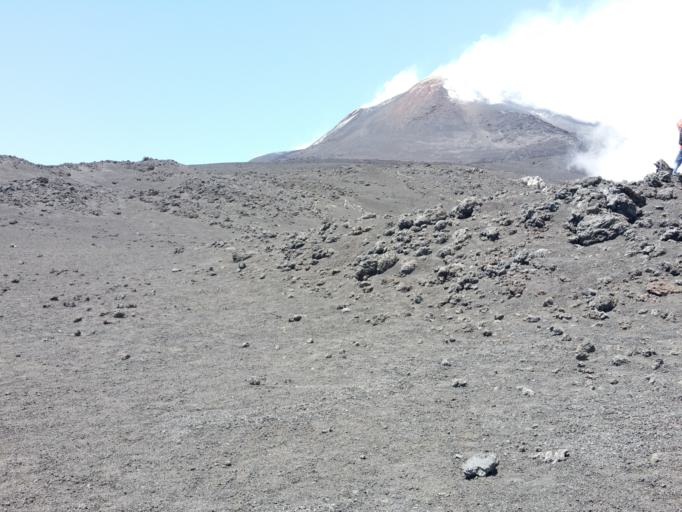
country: IT
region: Sicily
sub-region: Catania
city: Milo
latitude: 37.7334
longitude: 15.0098
